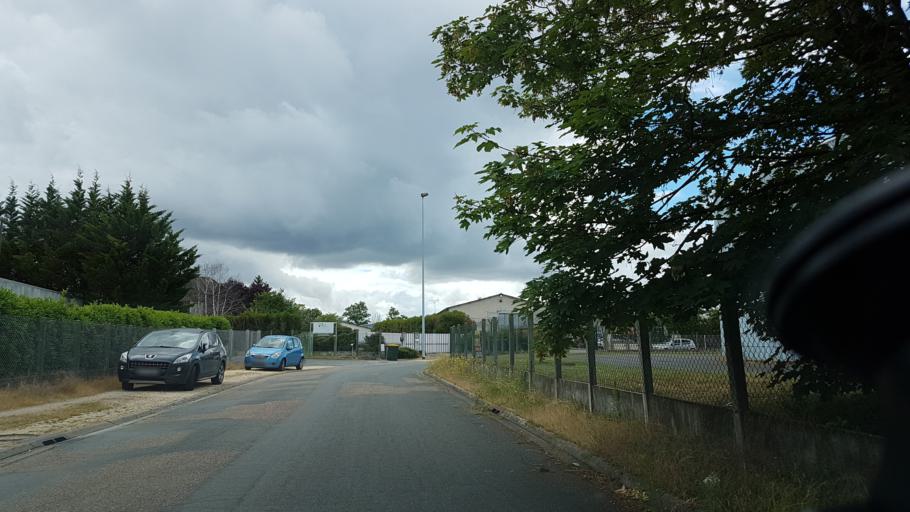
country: FR
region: Centre
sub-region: Departement du Cher
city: Bourges
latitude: 47.1061
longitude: 2.3865
